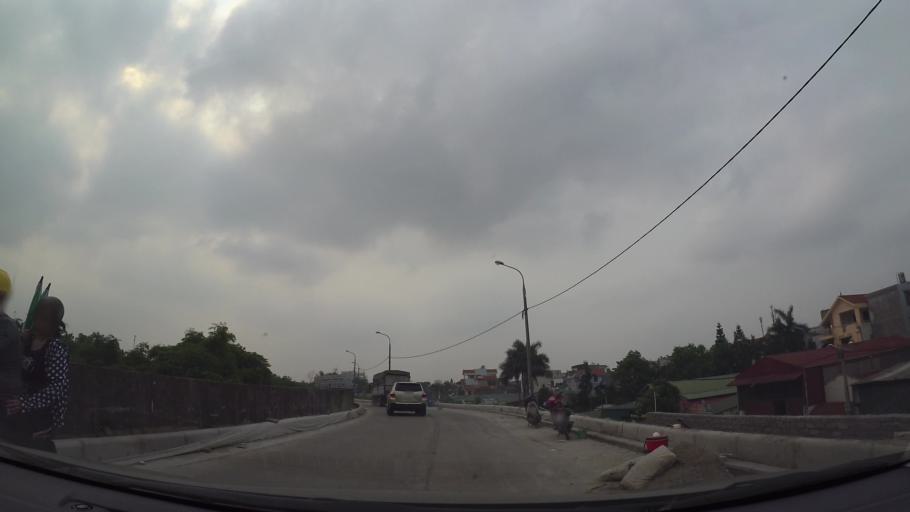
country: VN
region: Ha Noi
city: Trau Quy
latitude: 21.0192
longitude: 105.9029
